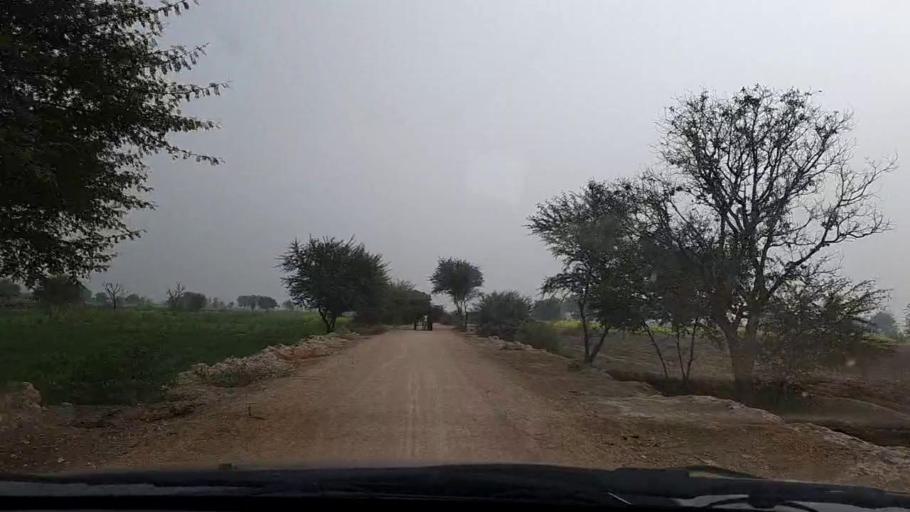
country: PK
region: Sindh
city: Pithoro
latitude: 25.7615
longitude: 69.3802
